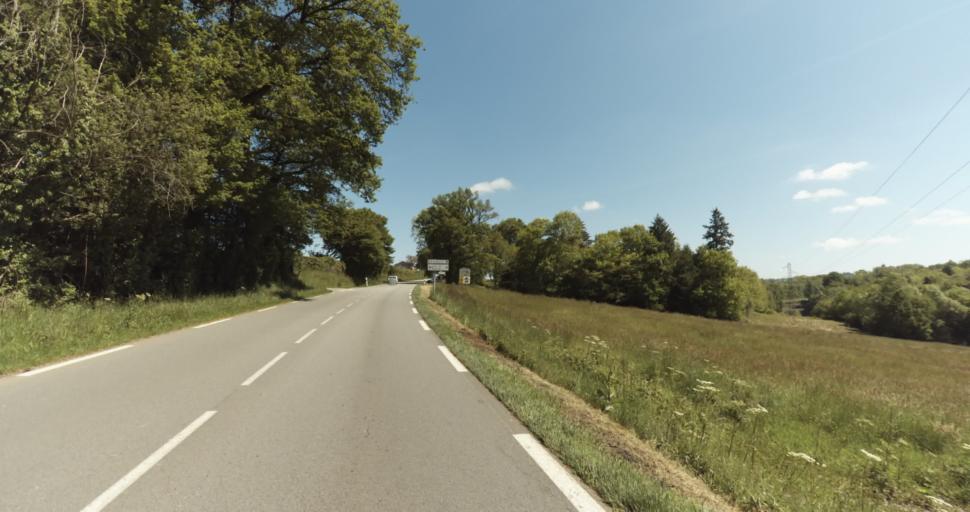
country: FR
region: Limousin
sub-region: Departement de la Haute-Vienne
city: Le Vigen
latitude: 45.7606
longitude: 1.2938
